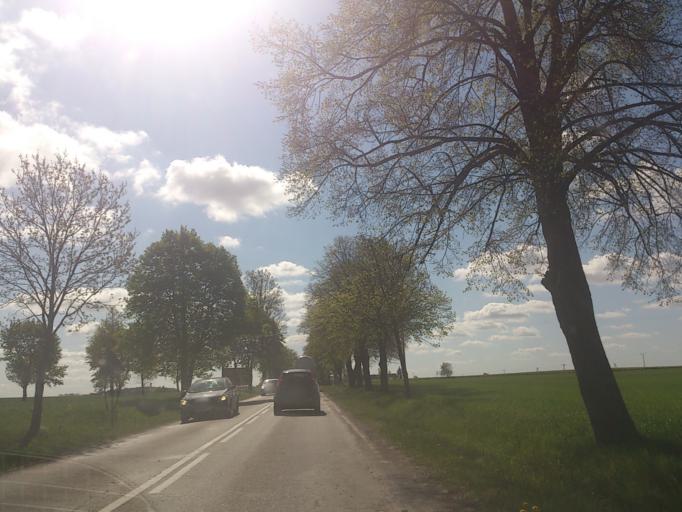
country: PL
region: Warmian-Masurian Voivodeship
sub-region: Powiat dzialdowski
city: Ilowo -Osada
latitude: 53.2048
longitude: 20.2392
